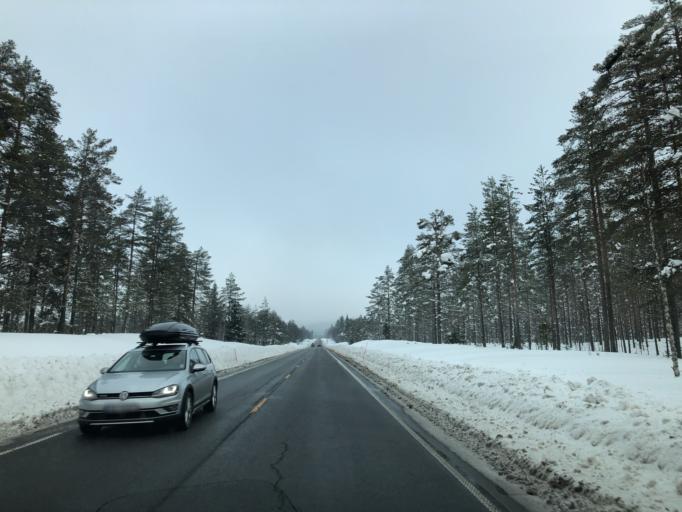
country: NO
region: Hedmark
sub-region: Elverum
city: Elverum
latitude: 61.0313
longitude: 11.8656
